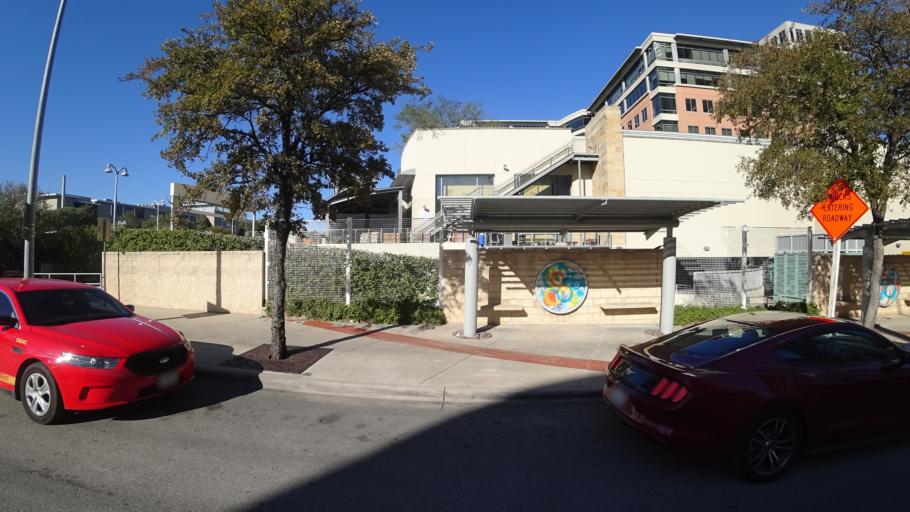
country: US
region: Texas
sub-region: Travis County
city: Austin
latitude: 30.2700
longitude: -97.7538
